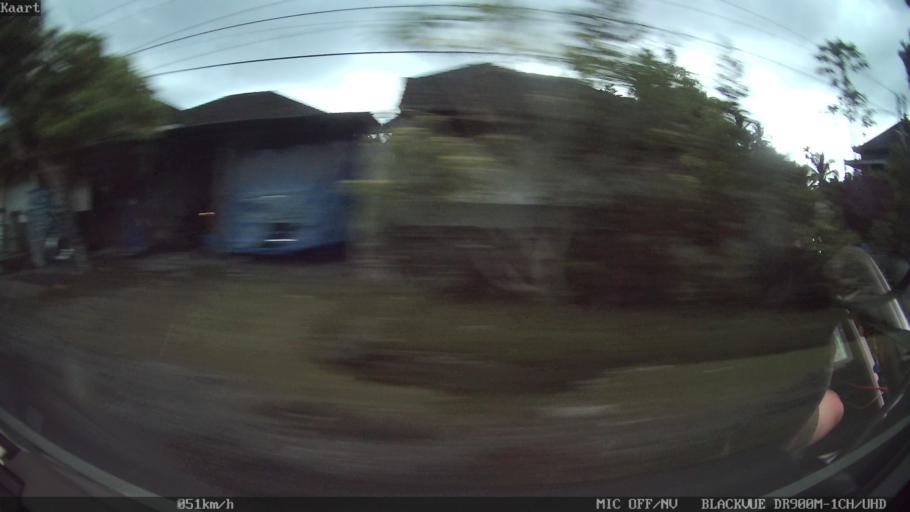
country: ID
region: Bali
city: Banjar Mandung
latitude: -8.5196
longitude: 115.0941
